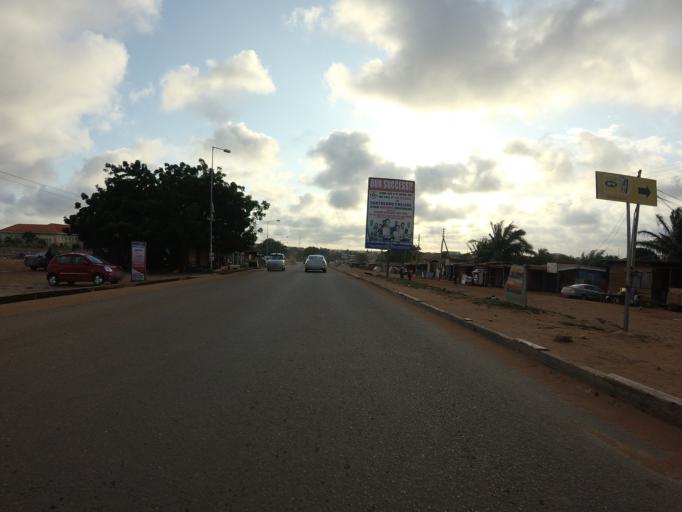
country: GH
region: Greater Accra
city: Teshi Old Town
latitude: 5.6049
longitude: -0.1187
